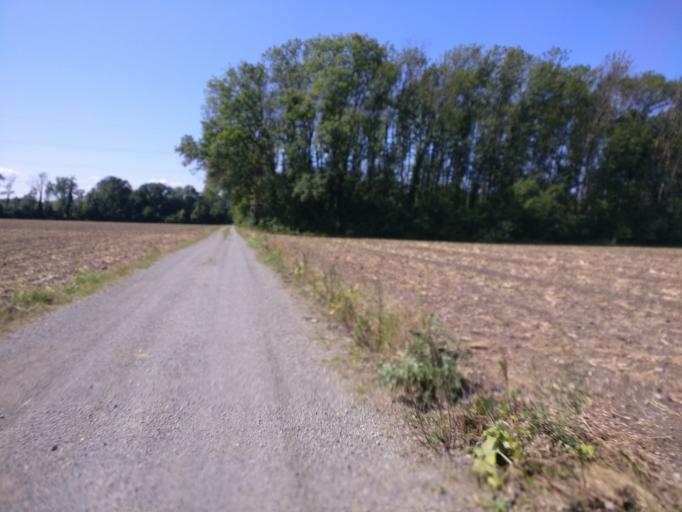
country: AT
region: Lower Austria
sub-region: Politischer Bezirk Baden
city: Pottendorf
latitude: 47.9278
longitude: 16.3684
